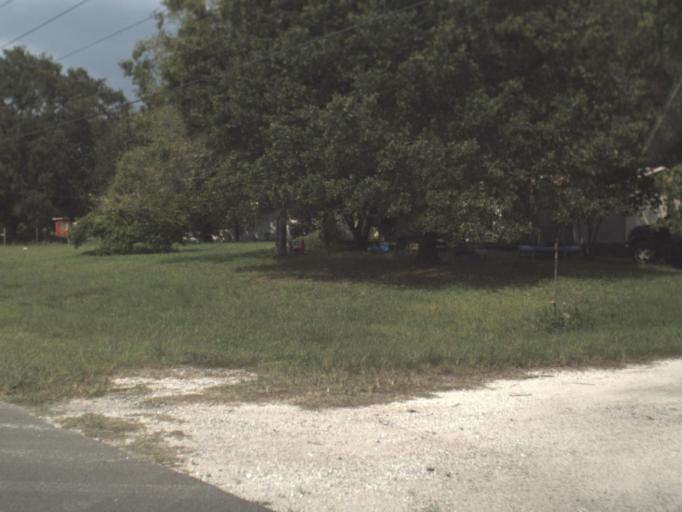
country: US
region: Florida
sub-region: Pasco County
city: Shady Hills
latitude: 28.3597
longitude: -82.5032
